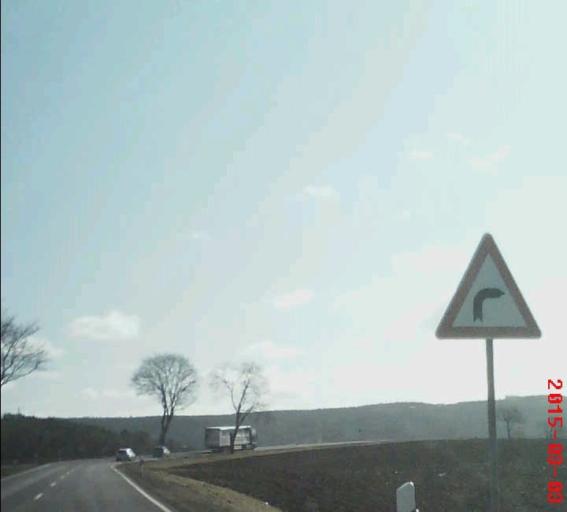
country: DE
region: Thuringia
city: Stadtilm
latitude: 50.7874
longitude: 11.0592
